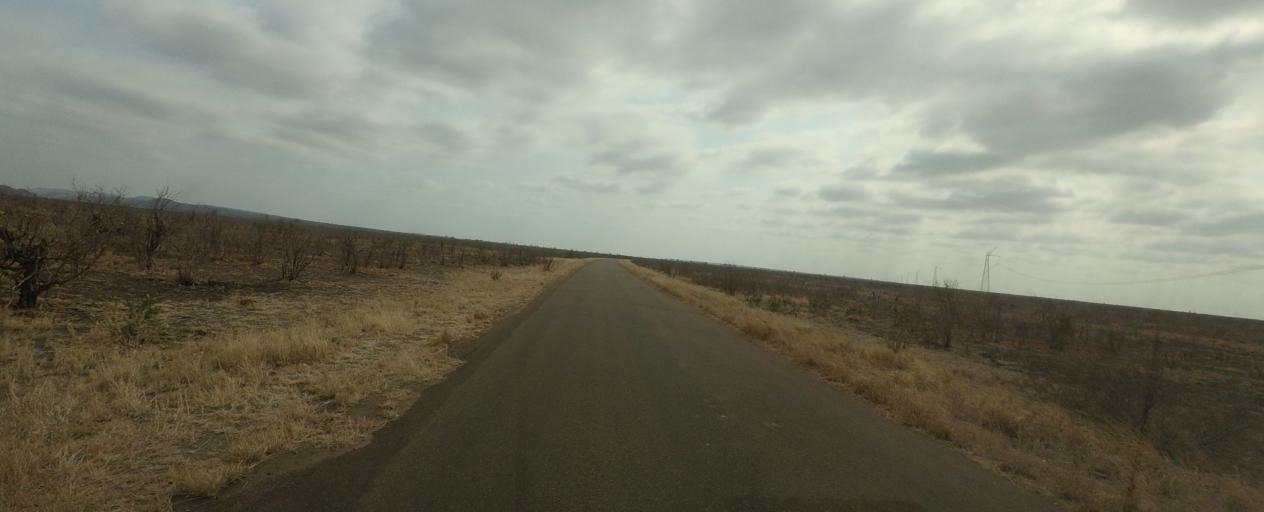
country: ZA
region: Limpopo
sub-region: Vhembe District Municipality
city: Mutale
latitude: -22.6559
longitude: 31.1700
